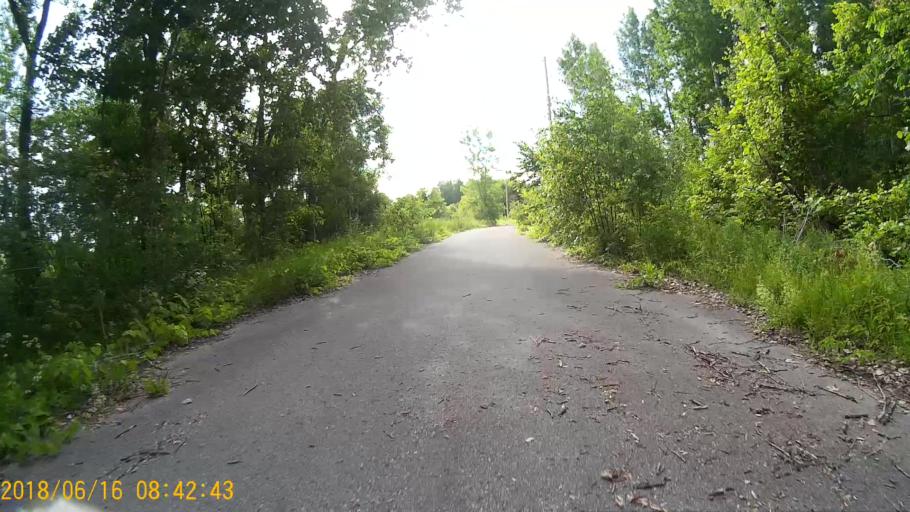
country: CA
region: Ontario
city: Bells Corners
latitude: 45.3505
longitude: -75.9050
